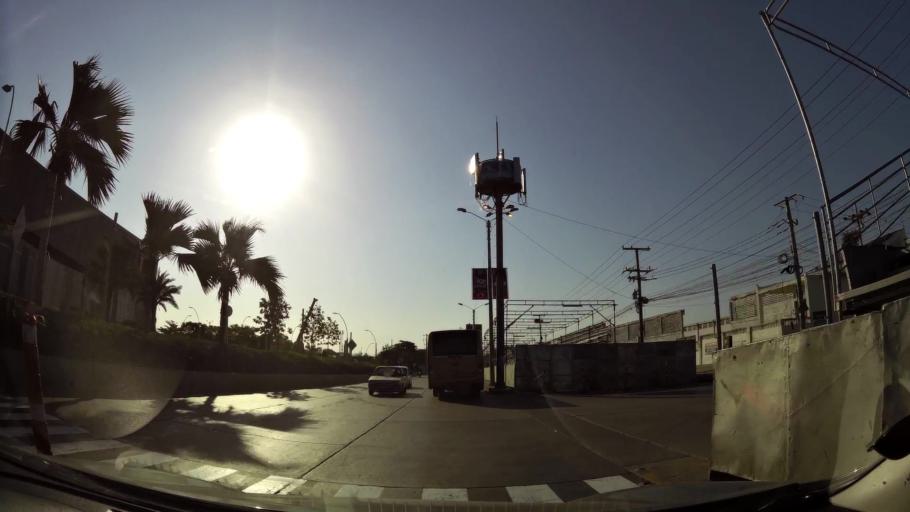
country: CO
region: Atlantico
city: Barranquilla
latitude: 11.0231
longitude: -74.8008
